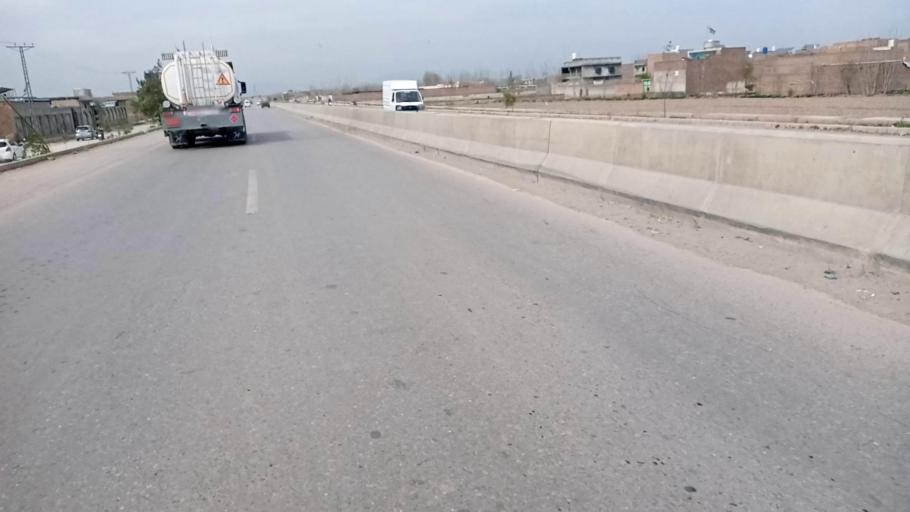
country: PK
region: Khyber Pakhtunkhwa
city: Peshawar
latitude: 34.0410
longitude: 71.6183
